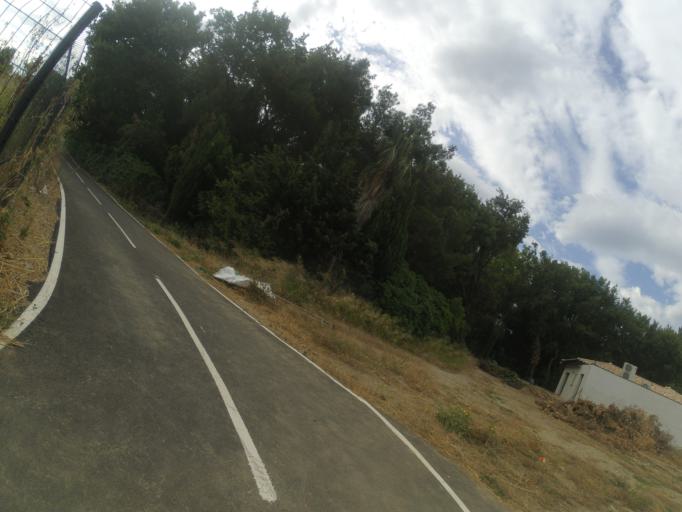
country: FR
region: Languedoc-Roussillon
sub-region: Departement des Pyrenees-Orientales
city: Toulouges
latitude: 42.6764
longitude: 2.8335
